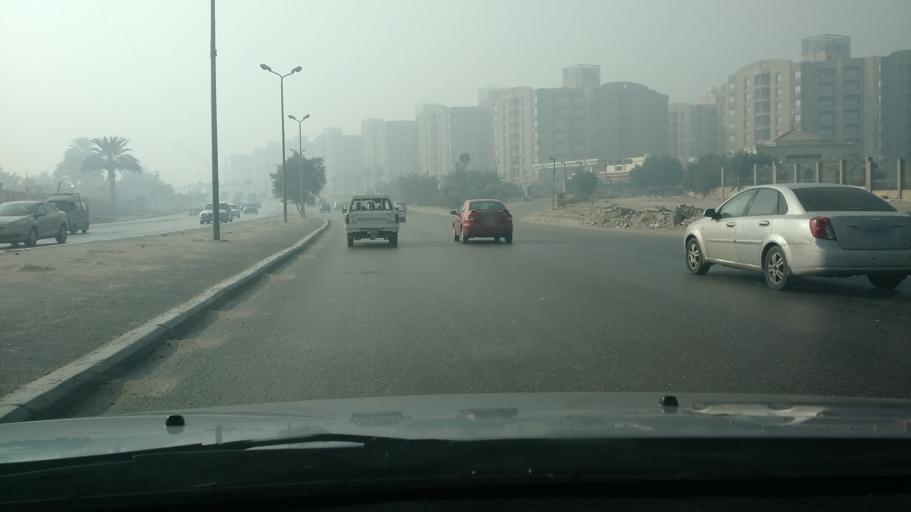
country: EG
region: Al Jizah
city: Al Hawamidiyah
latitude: 29.9692
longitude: 31.2886
